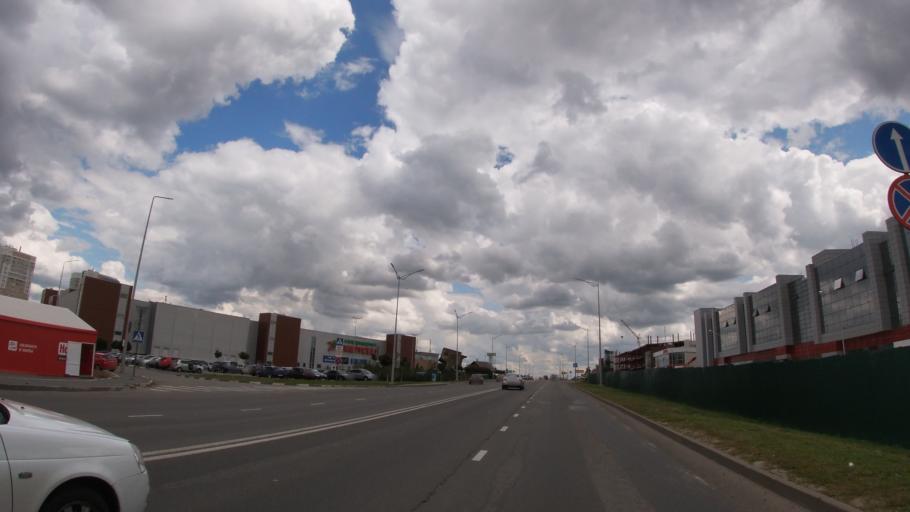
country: RU
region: Belgorod
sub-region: Belgorodskiy Rayon
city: Belgorod
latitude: 50.5510
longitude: 36.5656
